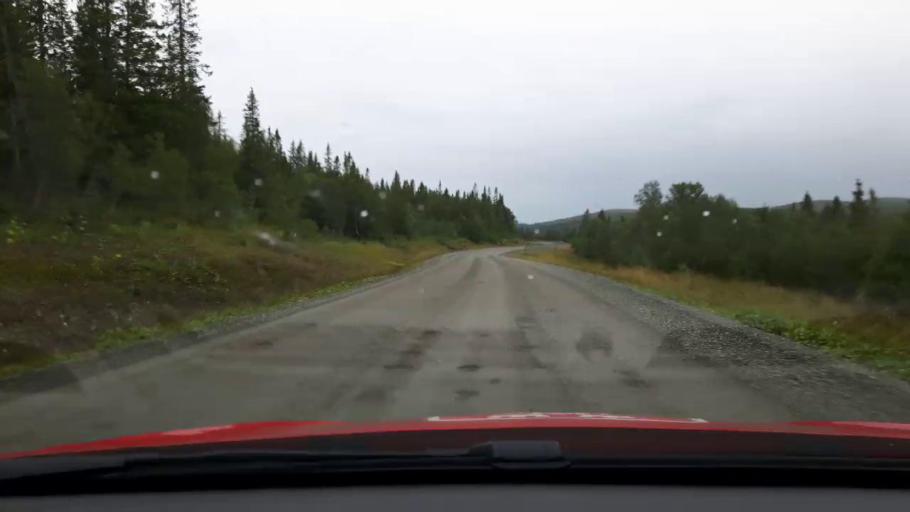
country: NO
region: Nord-Trondelag
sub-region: Meraker
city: Meraker
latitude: 63.5401
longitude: 12.3815
